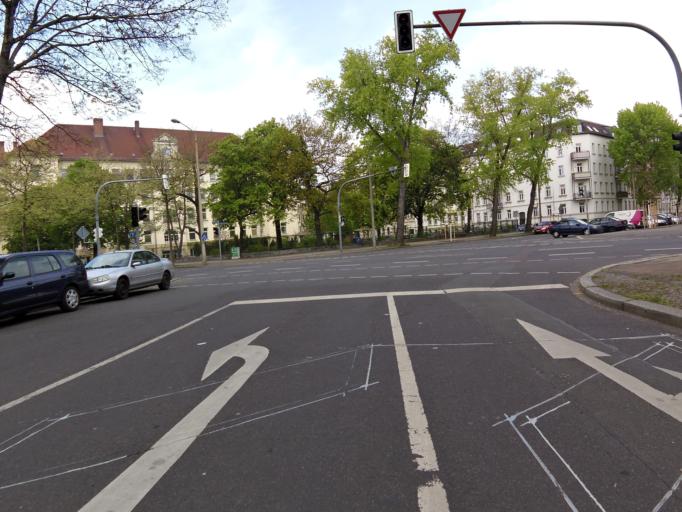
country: DE
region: Saxony
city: Leipzig
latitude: 51.3615
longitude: 12.3901
